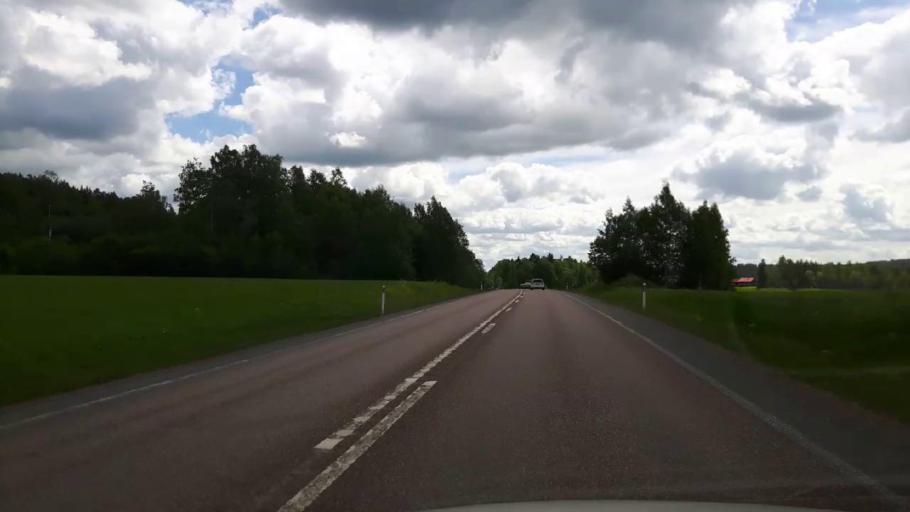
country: SE
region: Dalarna
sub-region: Saters Kommun
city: Saeter
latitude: 60.4837
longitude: 15.7713
